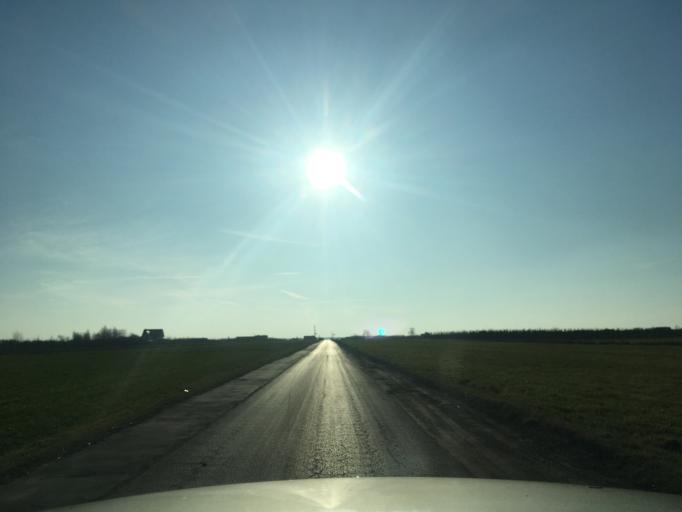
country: PL
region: Masovian Voivodeship
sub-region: Powiat pruszkowski
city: Nadarzyn
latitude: 52.0417
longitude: 20.8270
